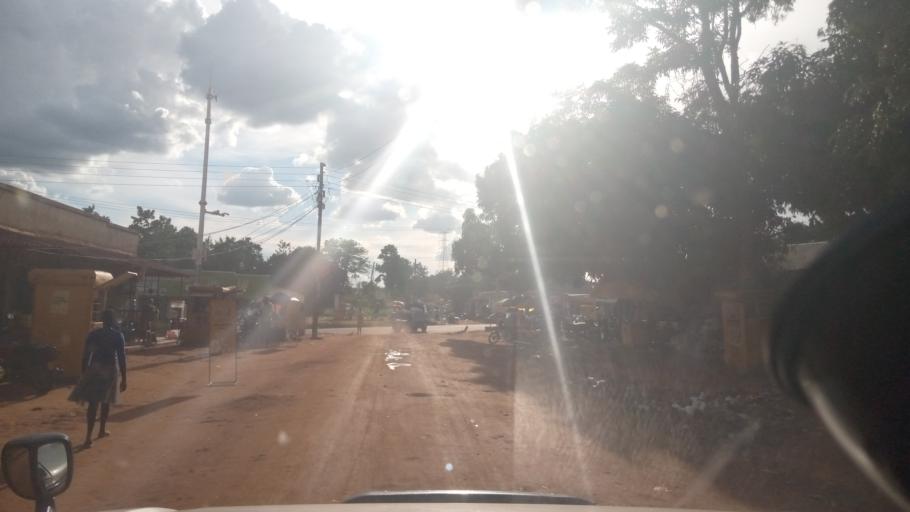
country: UG
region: Northern Region
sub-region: Lira District
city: Lira
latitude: 2.2275
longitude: 32.8958
